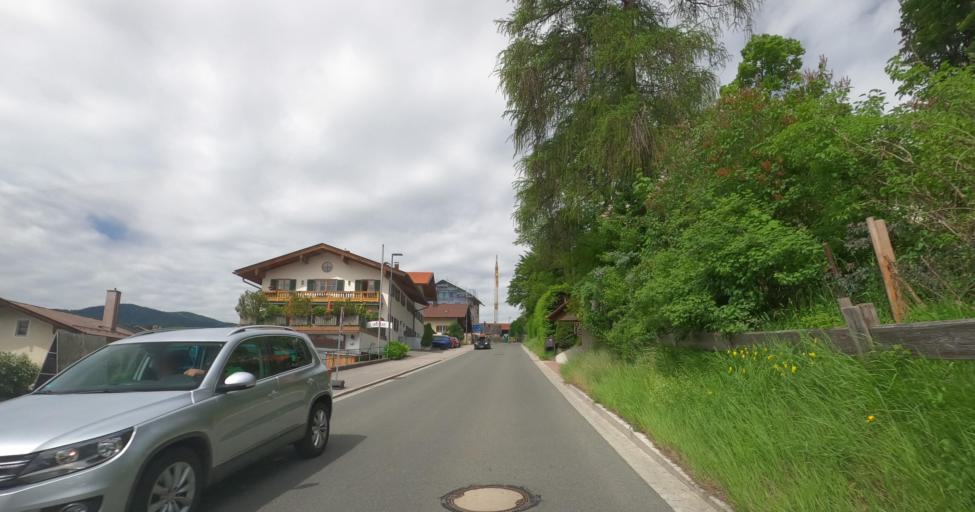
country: DE
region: Bavaria
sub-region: Upper Bavaria
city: Gmund am Tegernsee
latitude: 47.7510
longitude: 11.7358
